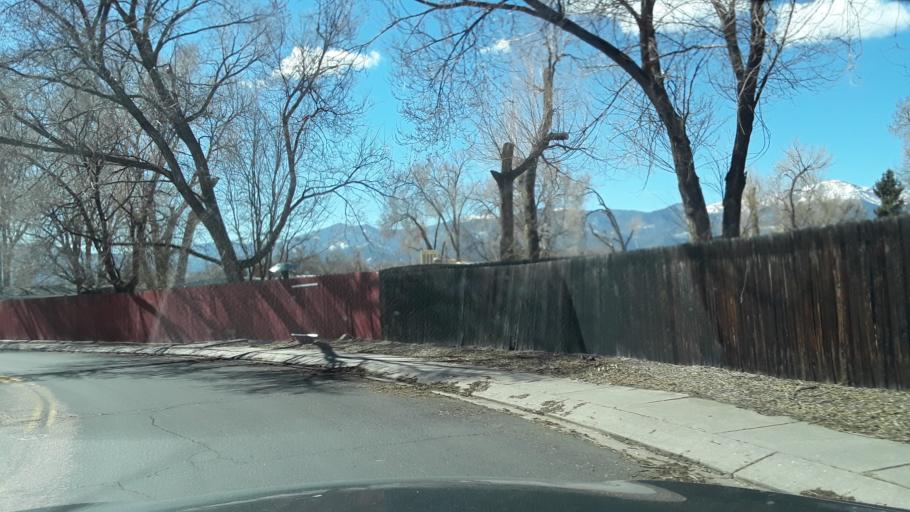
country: US
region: Colorado
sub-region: El Paso County
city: Colorado Springs
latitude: 38.8796
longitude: -104.8014
